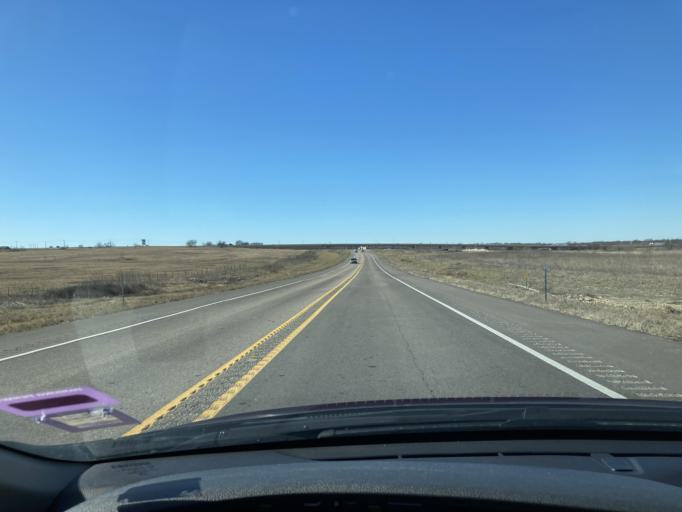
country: US
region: Texas
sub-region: Navarro County
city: Corsicana
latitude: 32.0439
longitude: -96.4388
